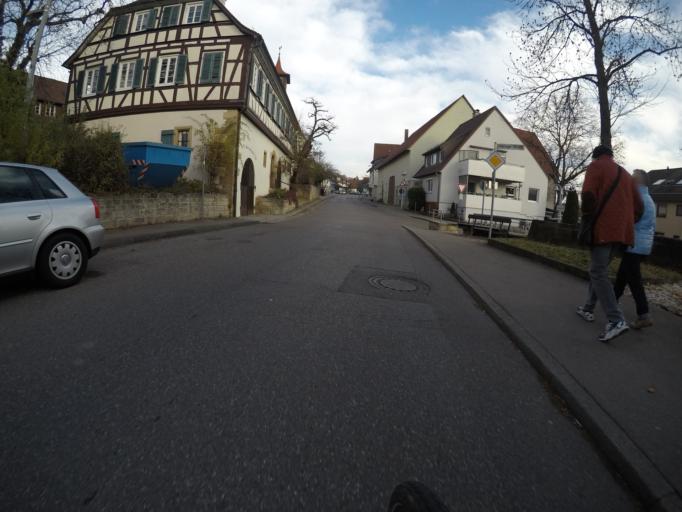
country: DE
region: Baden-Wuerttemberg
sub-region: Regierungsbezirk Stuttgart
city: Steinenbronn
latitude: 48.6918
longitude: 9.1211
